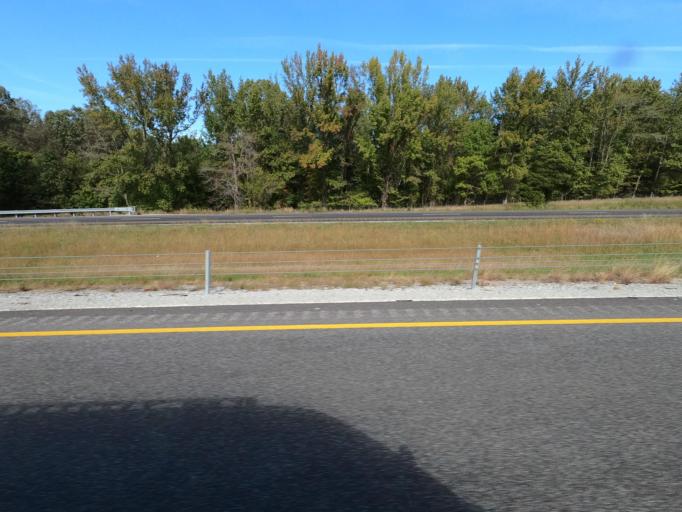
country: US
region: Tennessee
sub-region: Crockett County
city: Bells
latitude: 35.6120
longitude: -89.0155
